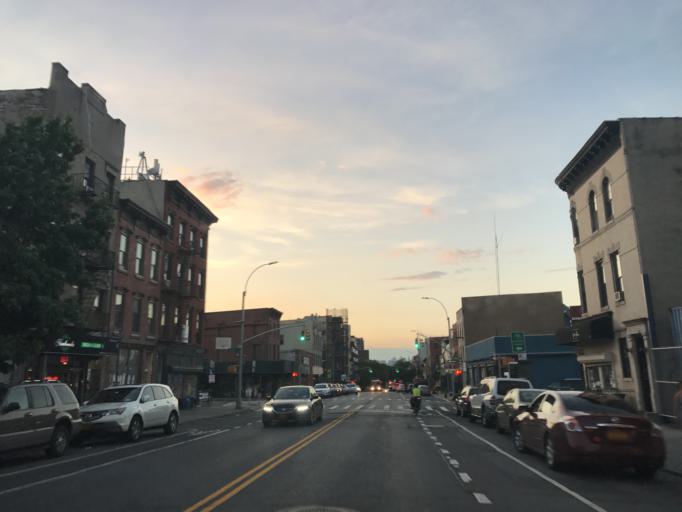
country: US
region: New York
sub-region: Kings County
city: Brooklyn
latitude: 40.6781
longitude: -73.9638
